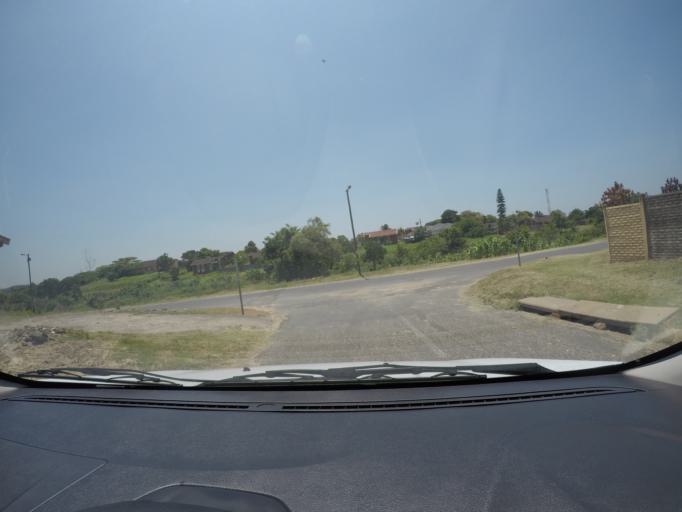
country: ZA
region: KwaZulu-Natal
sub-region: uThungulu District Municipality
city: eSikhawini
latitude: -28.8739
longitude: 31.9102
